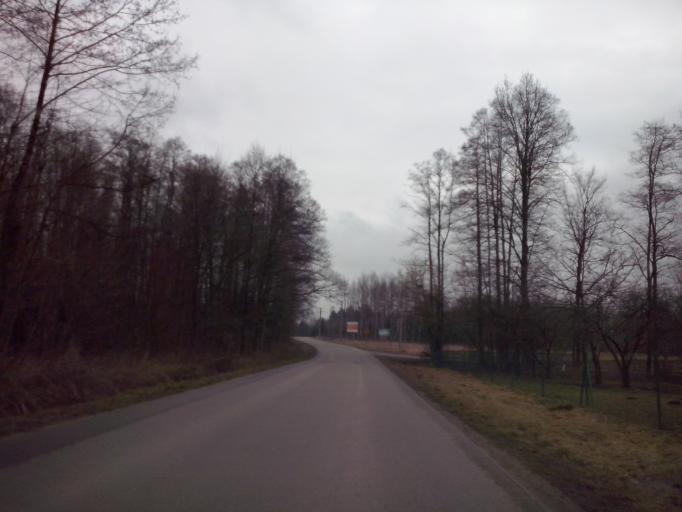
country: PL
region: Subcarpathian Voivodeship
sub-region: Powiat nizanski
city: Bieliny
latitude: 50.4285
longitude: 22.3113
